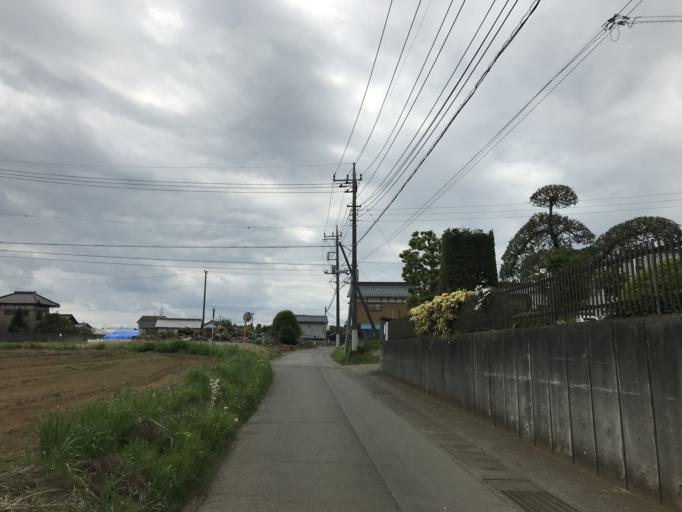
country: JP
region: Ibaraki
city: Mitsukaido
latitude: 36.0213
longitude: 140.0324
